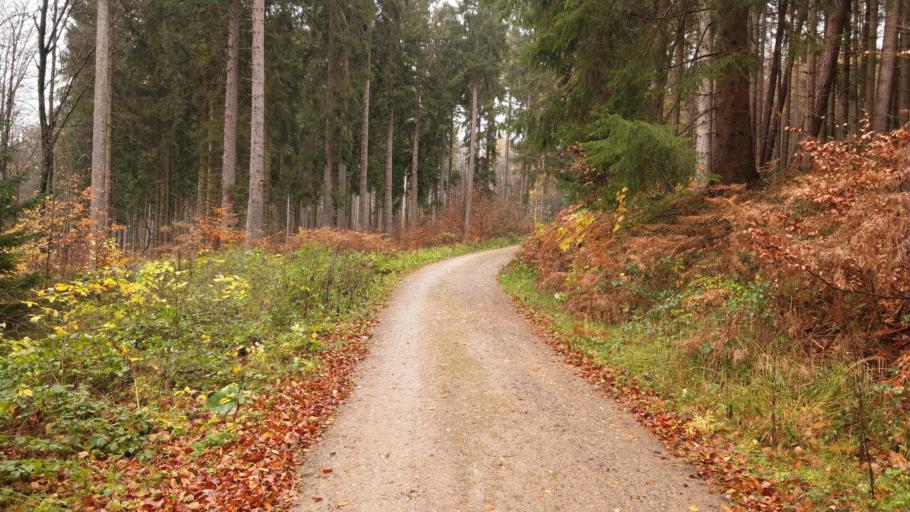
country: BE
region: Wallonia
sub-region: Province de Liege
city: La Calamine
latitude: 50.7328
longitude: 6.0526
